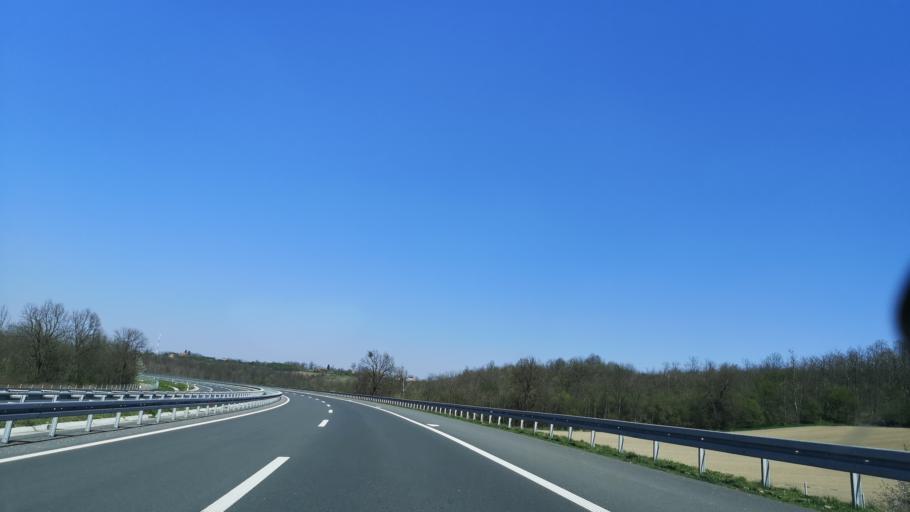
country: RS
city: Stubline
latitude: 44.5005
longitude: 20.1469
